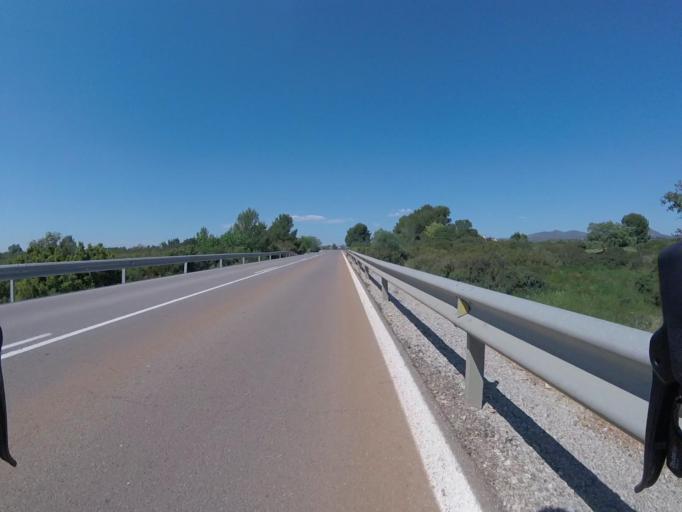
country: ES
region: Valencia
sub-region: Provincia de Castello
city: Benlloch
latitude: 40.2030
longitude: 0.0024
